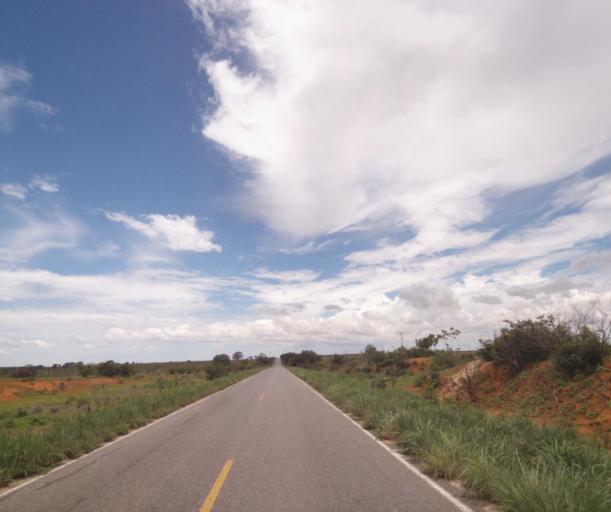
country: BR
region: Bahia
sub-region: Carinhanha
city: Carinhanha
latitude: -14.2880
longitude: -43.6261
